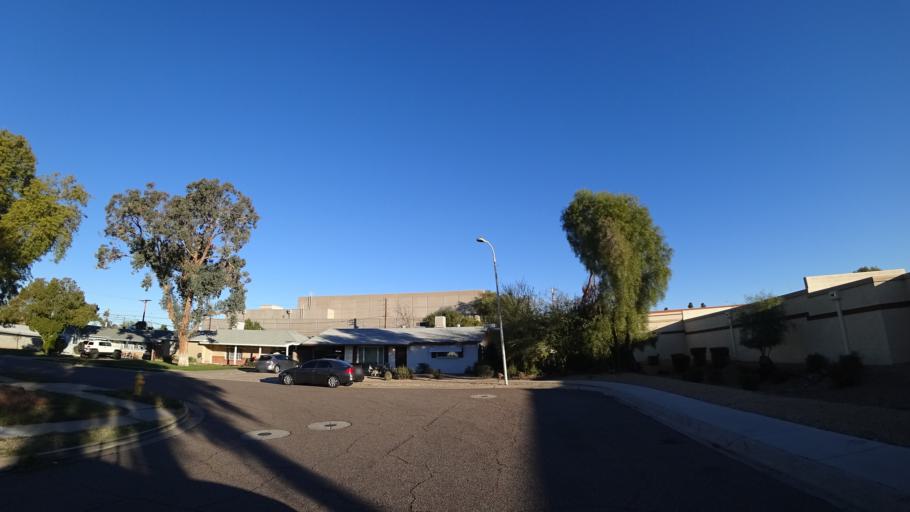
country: US
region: Arizona
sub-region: Maricopa County
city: Paradise Valley
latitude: 33.4939
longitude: -112.0075
